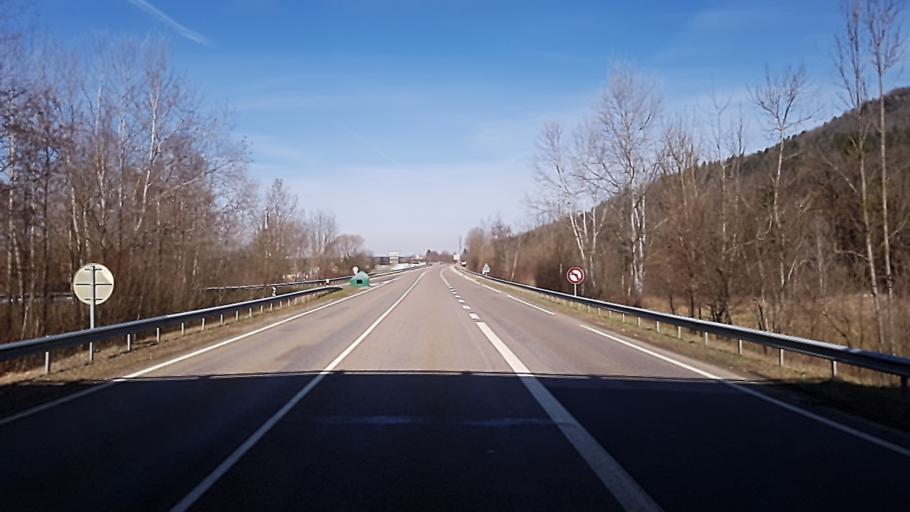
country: FR
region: Franche-Comte
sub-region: Departement du Jura
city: Champagnole
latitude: 46.7456
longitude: 5.9258
